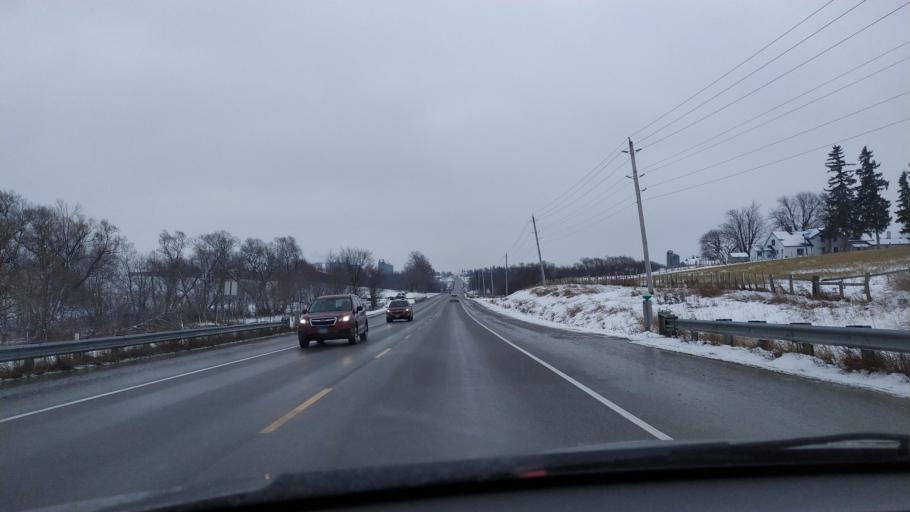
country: CA
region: Ontario
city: Waterloo
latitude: 43.6066
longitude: -80.6520
